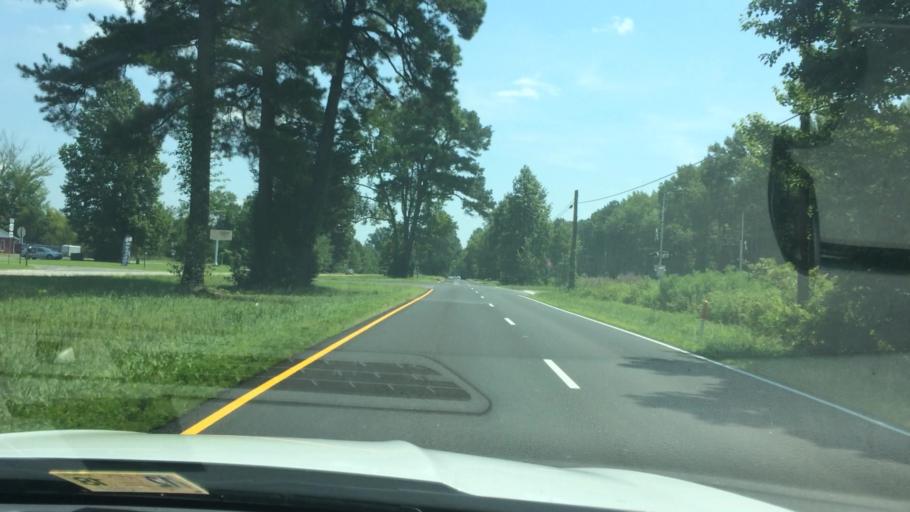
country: US
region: Virginia
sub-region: Charles City County
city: Charles City
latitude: 37.4459
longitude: -77.0599
